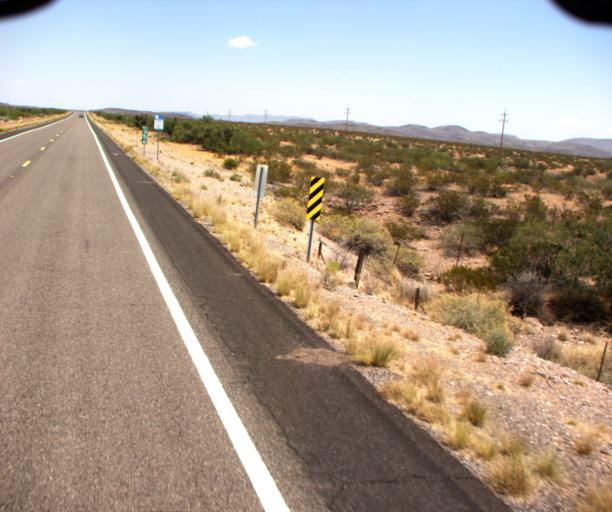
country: US
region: Arizona
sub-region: Graham County
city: Swift Trail Junction
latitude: 32.7625
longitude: -109.4461
